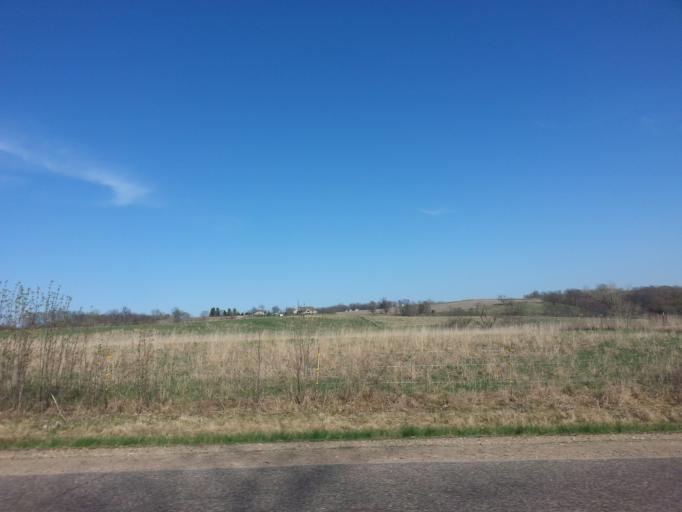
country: US
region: Wisconsin
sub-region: Pierce County
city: Ellsworth
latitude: 44.7689
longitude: -92.5782
